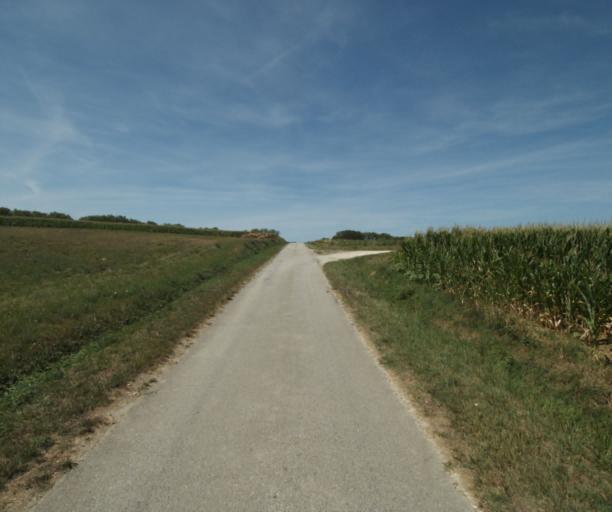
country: FR
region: Midi-Pyrenees
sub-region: Departement de la Haute-Garonne
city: Revel
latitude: 43.4948
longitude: 2.0165
